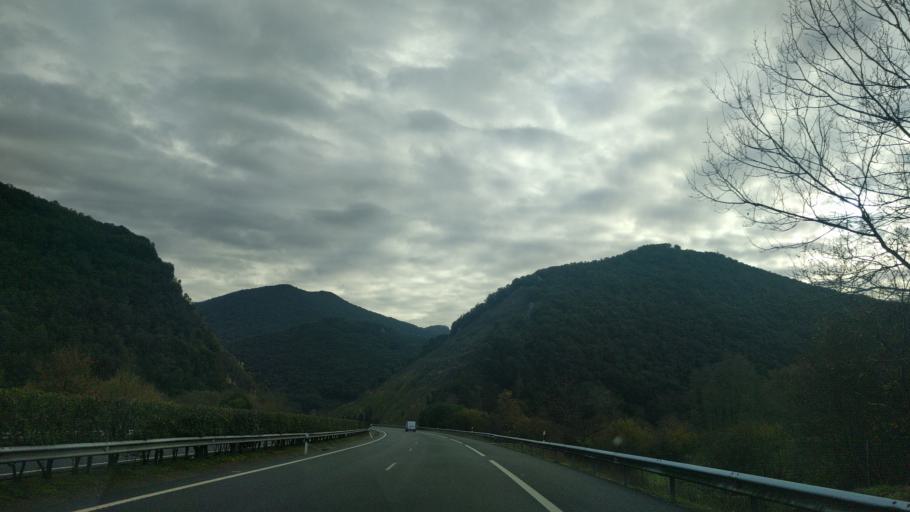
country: ES
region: Cantabria
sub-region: Provincia de Cantabria
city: Liendo
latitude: 43.3814
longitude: -3.3793
